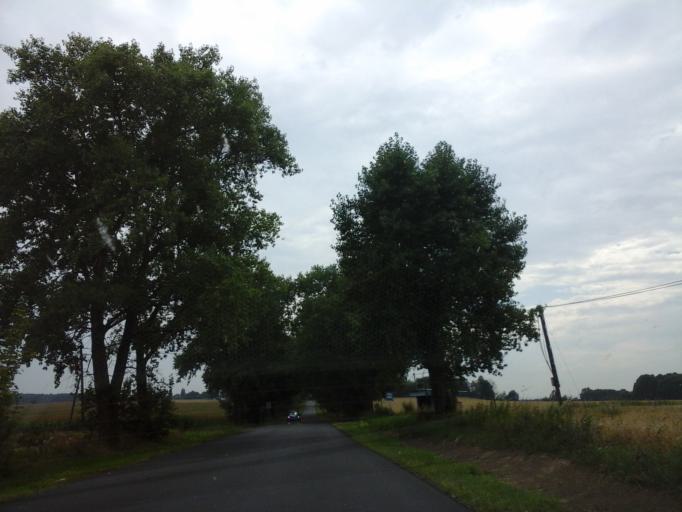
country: PL
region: Lower Silesian Voivodeship
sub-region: Powiat zabkowicki
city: Cieplowody
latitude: 50.6448
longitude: 16.8917
